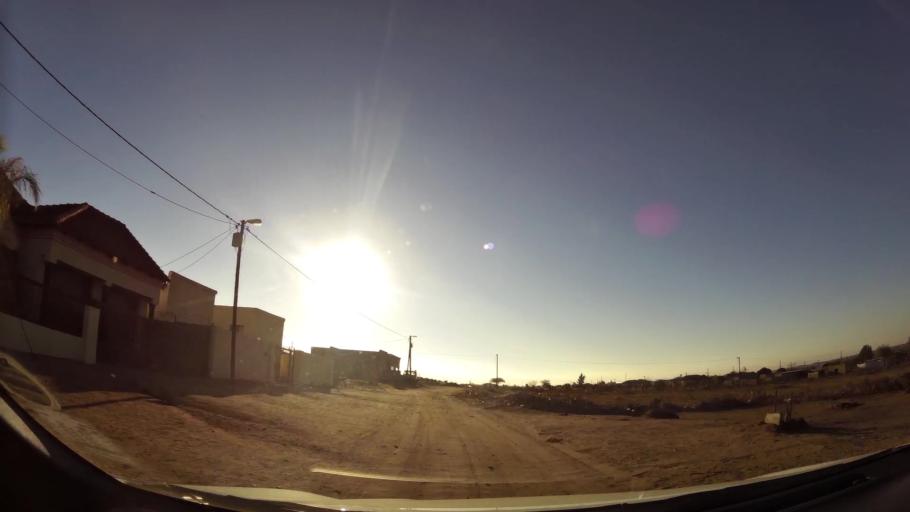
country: ZA
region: Limpopo
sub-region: Capricorn District Municipality
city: Polokwane
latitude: -23.8383
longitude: 29.3582
